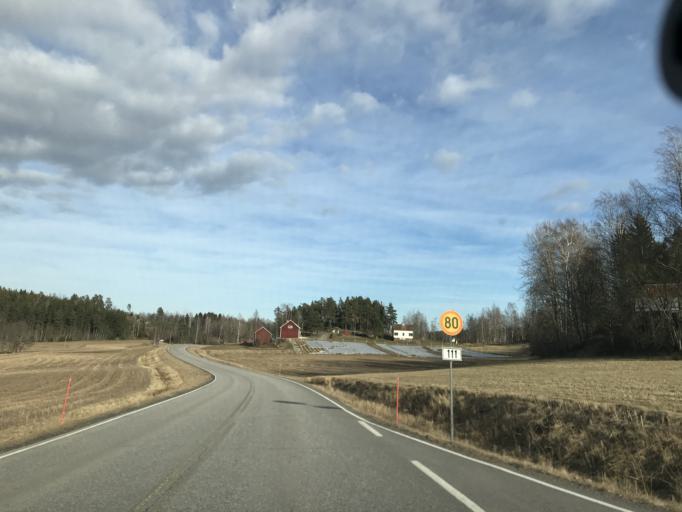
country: FI
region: Uusimaa
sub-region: Raaseporin
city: Ekenaes
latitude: 60.0752
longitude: 23.3396
